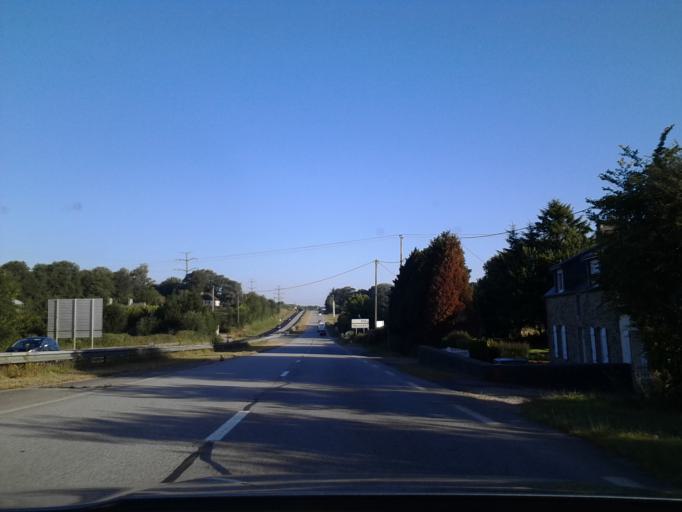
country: FR
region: Lower Normandy
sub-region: Departement de la Manche
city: La Glacerie
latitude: 49.5786
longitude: -1.5832
